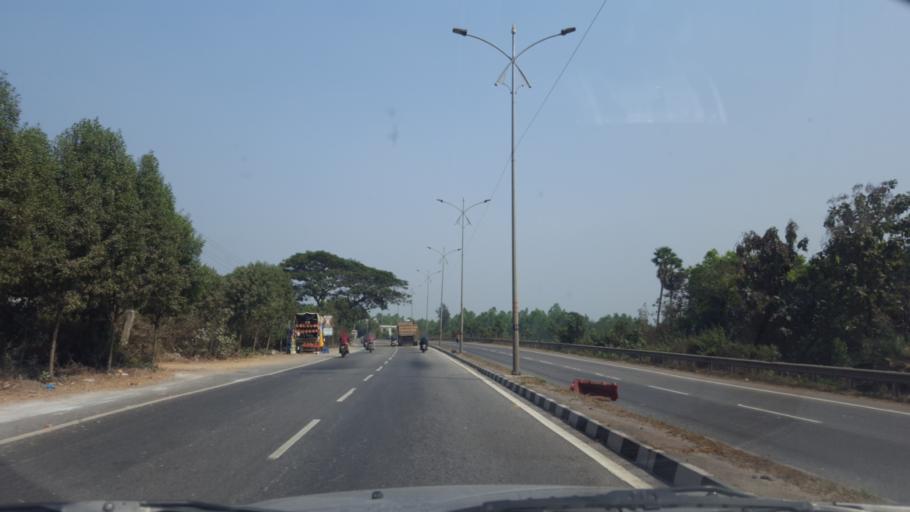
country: IN
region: Andhra Pradesh
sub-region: Vishakhapatnam
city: Anakapalle
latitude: 17.6887
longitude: 83.0683
